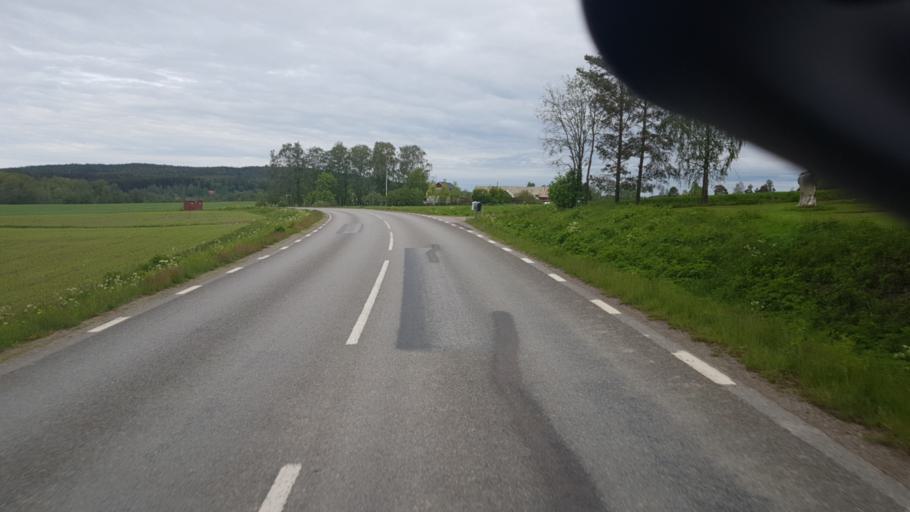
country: SE
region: Vaermland
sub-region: Arvika Kommun
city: Arvika
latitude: 59.7502
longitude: 12.5538
